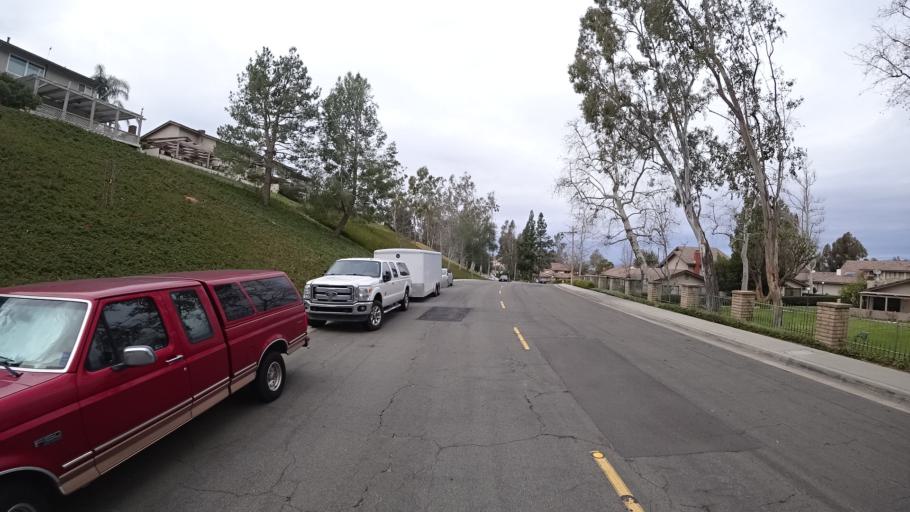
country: US
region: California
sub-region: Orange County
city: Villa Park
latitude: 33.8356
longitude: -117.7612
